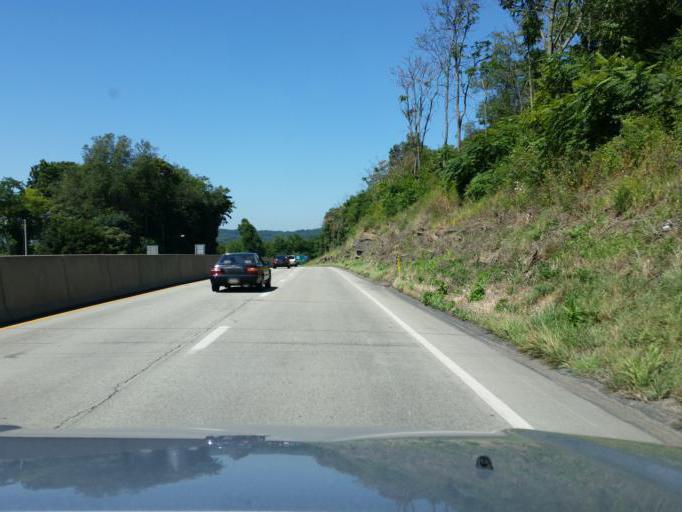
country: US
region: Pennsylvania
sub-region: Indiana County
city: Blairsville
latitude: 40.4399
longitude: -79.2653
